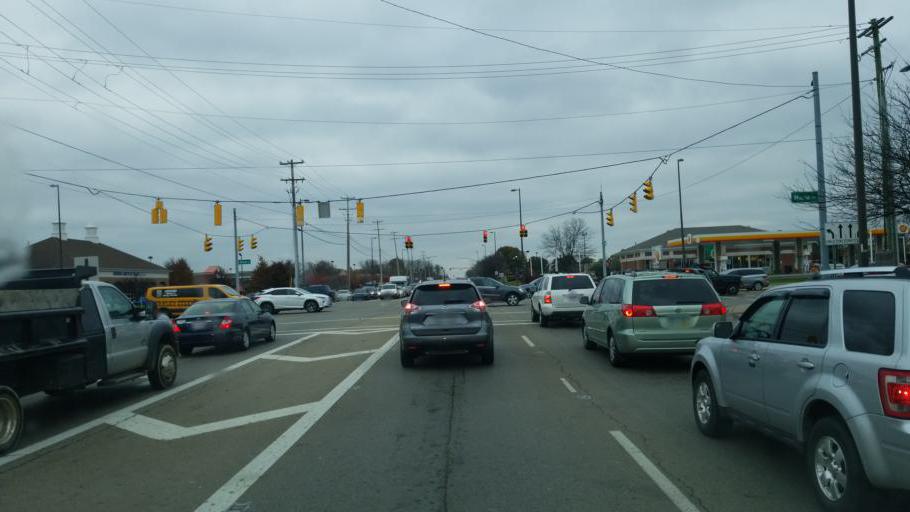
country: US
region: Ohio
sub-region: Franklin County
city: Gahanna
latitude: 40.0558
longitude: -82.8637
